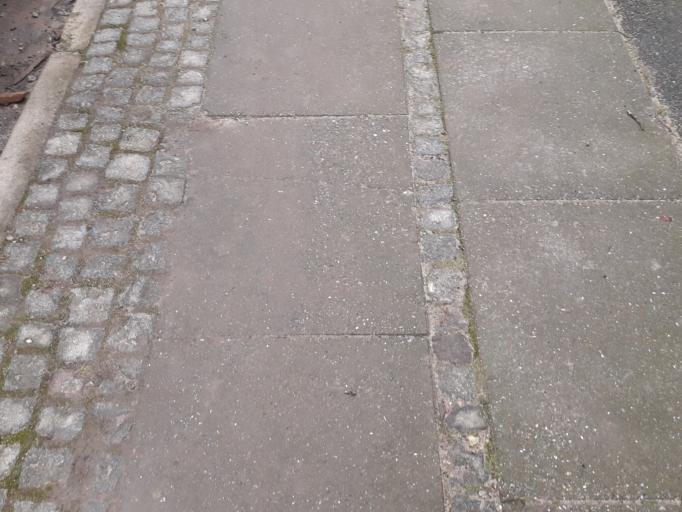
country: DK
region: Central Jutland
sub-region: Horsens Kommune
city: Horsens
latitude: 55.8560
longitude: 9.8330
